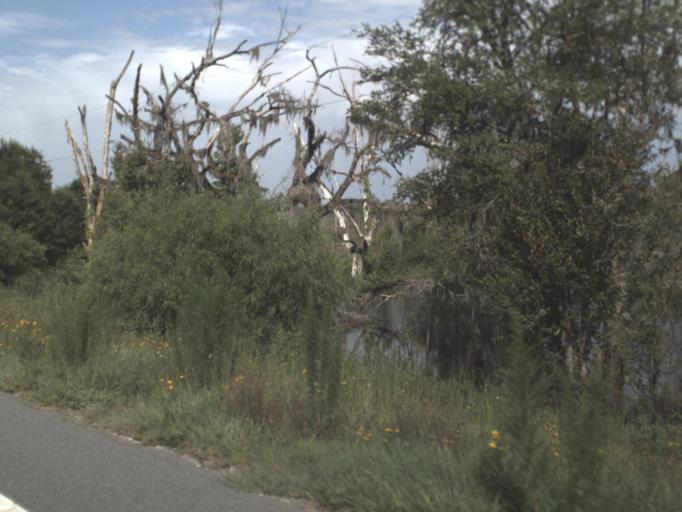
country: US
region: Florida
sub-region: Madison County
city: Madison
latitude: 30.6234
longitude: -83.3231
